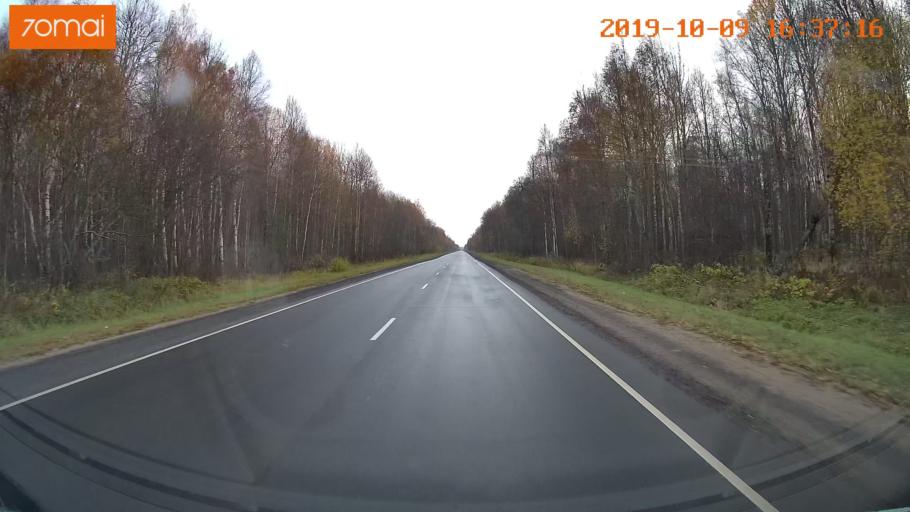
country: RU
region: Kostroma
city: Volgorechensk
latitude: 57.5294
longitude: 41.0226
